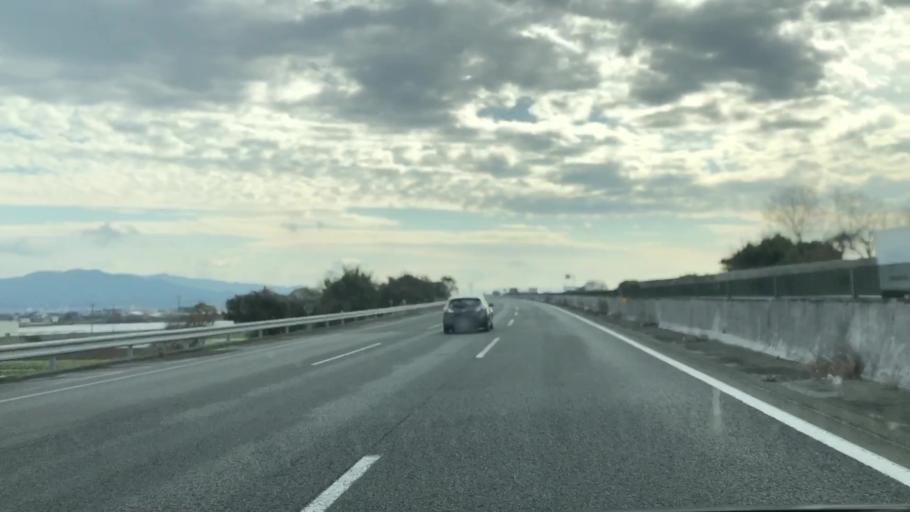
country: JP
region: Saga Prefecture
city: Tosu
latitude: 33.3506
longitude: 130.5377
